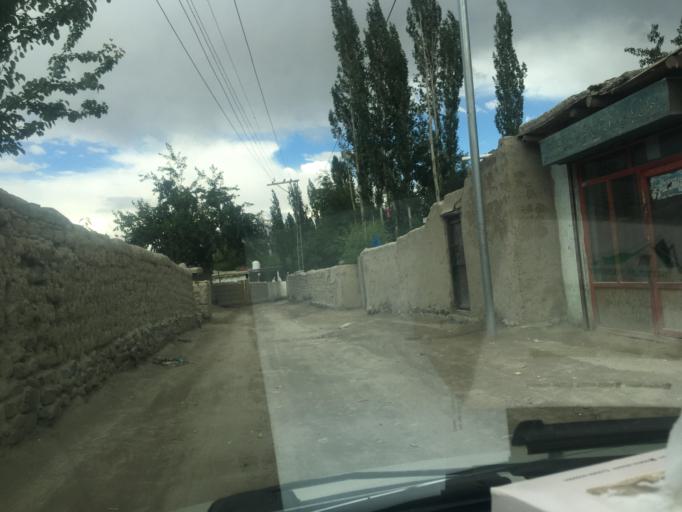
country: PK
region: Gilgit-Baltistan
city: Skardu
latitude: 35.3165
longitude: 75.5477
